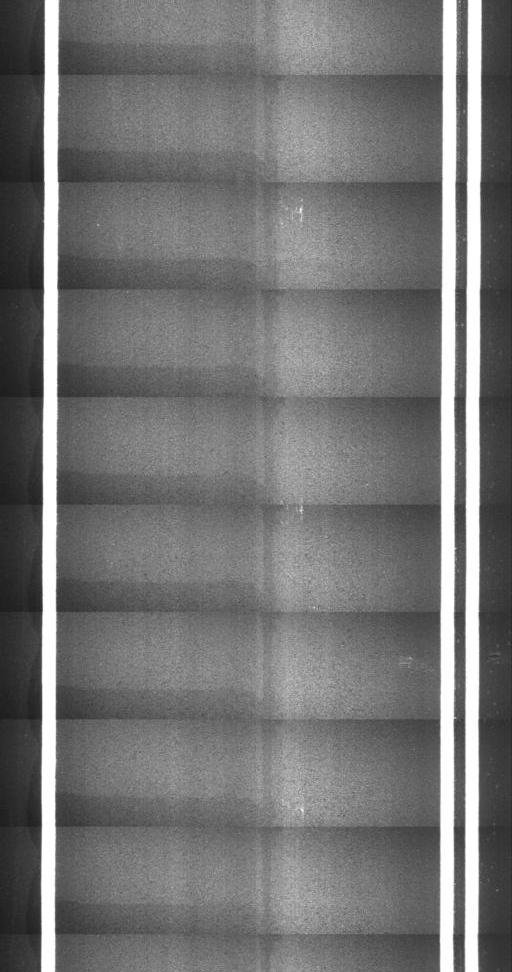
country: US
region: Vermont
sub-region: Caledonia County
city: Lyndonville
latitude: 44.5914
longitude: -71.9386
